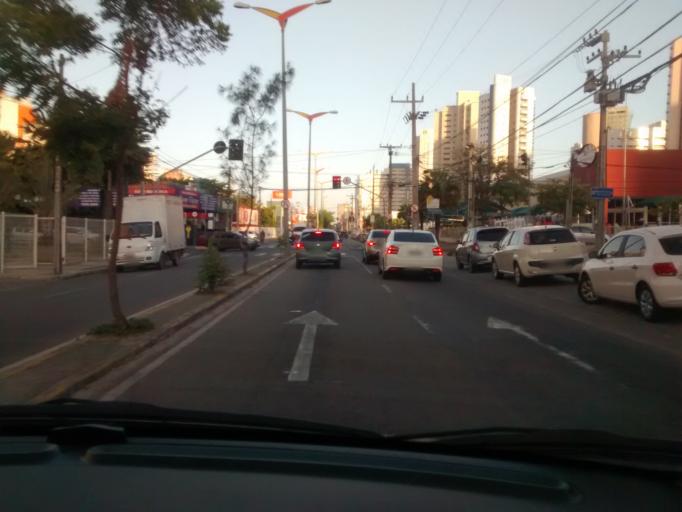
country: BR
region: Ceara
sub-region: Fortaleza
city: Fortaleza
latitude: -3.7422
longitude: -38.4801
